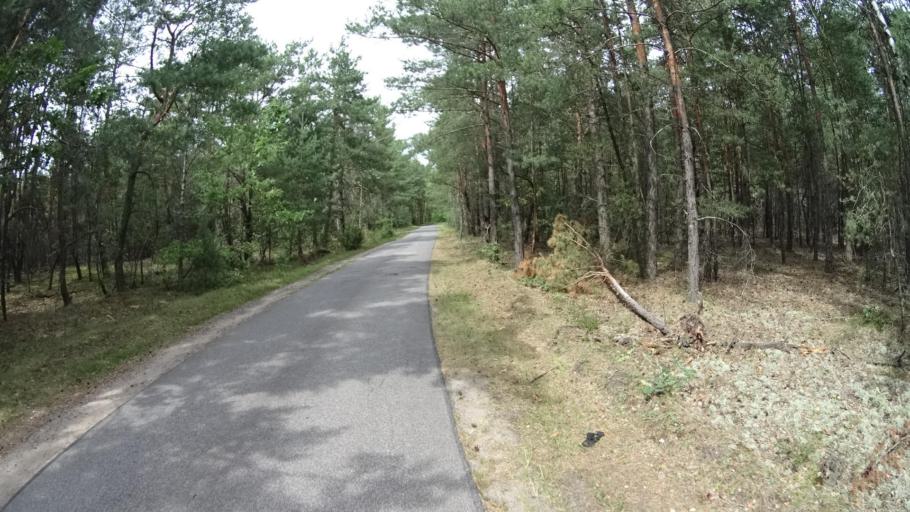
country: PL
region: Masovian Voivodeship
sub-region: Powiat bialobrzeski
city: Bialobrzegi
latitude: 51.6378
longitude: 20.9024
